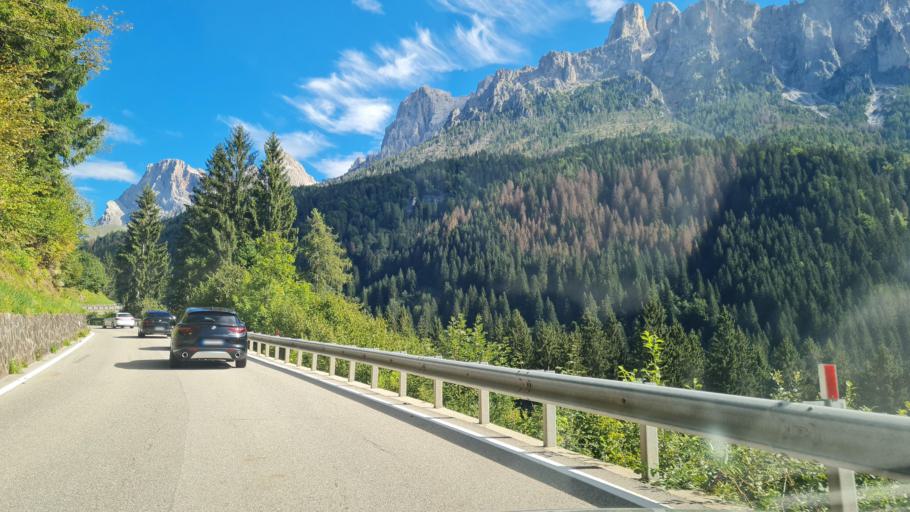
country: IT
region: Trentino-Alto Adige
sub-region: Provincia di Trento
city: Siror
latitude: 46.2088
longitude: 11.8175
